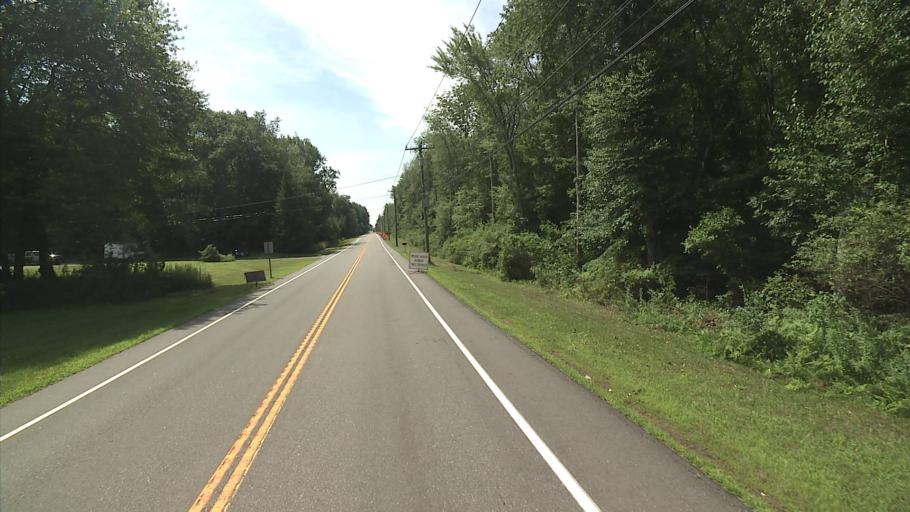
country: US
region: Connecticut
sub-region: Tolland County
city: Tolland
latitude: 41.8165
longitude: -72.3968
